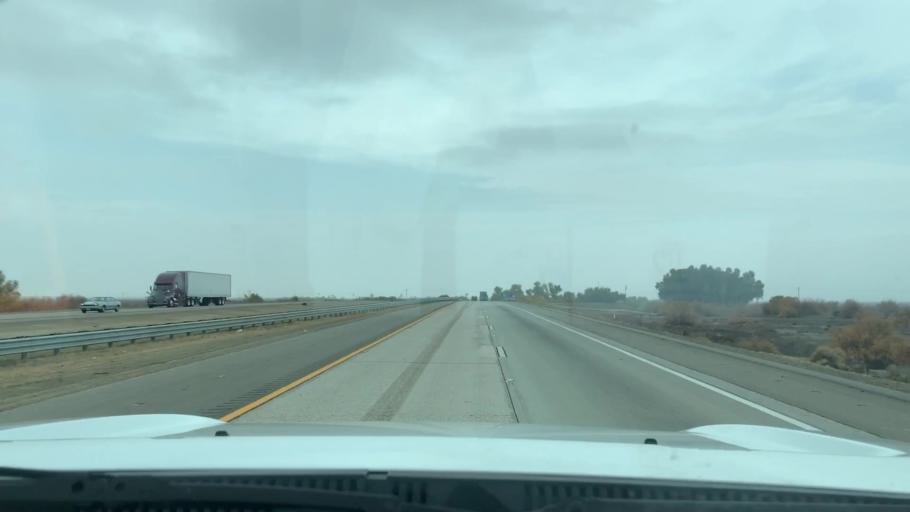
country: US
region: California
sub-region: Kern County
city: Lost Hills
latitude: 35.5977
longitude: -119.6374
